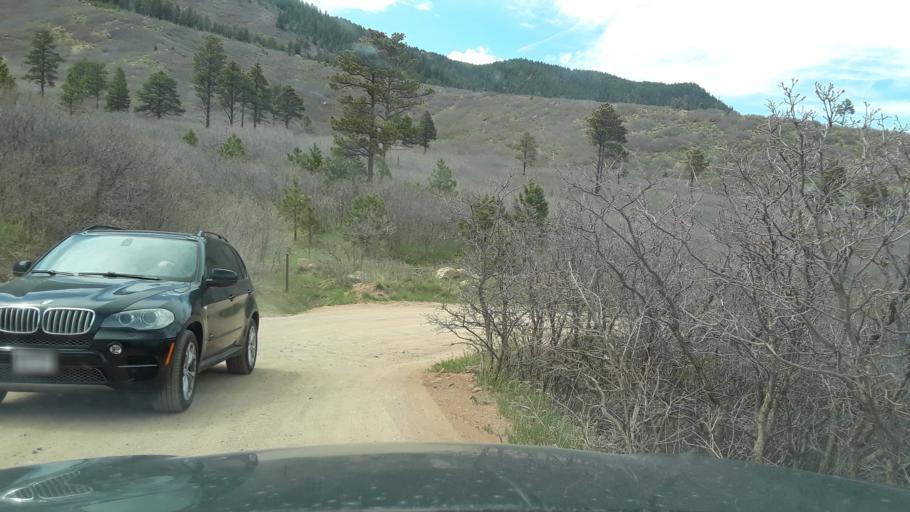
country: US
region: Colorado
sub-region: El Paso County
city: Palmer Lake
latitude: 39.0819
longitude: -104.9145
